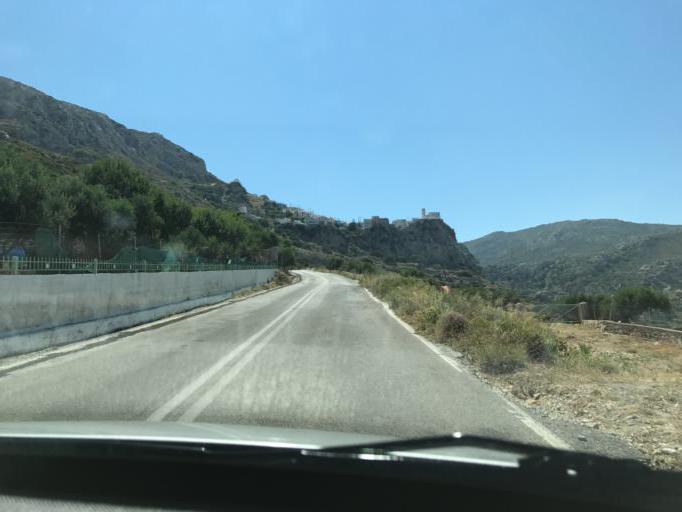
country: GR
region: South Aegean
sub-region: Nomos Dodekanisou
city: Karpathos
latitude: 35.4906
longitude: 27.1757
